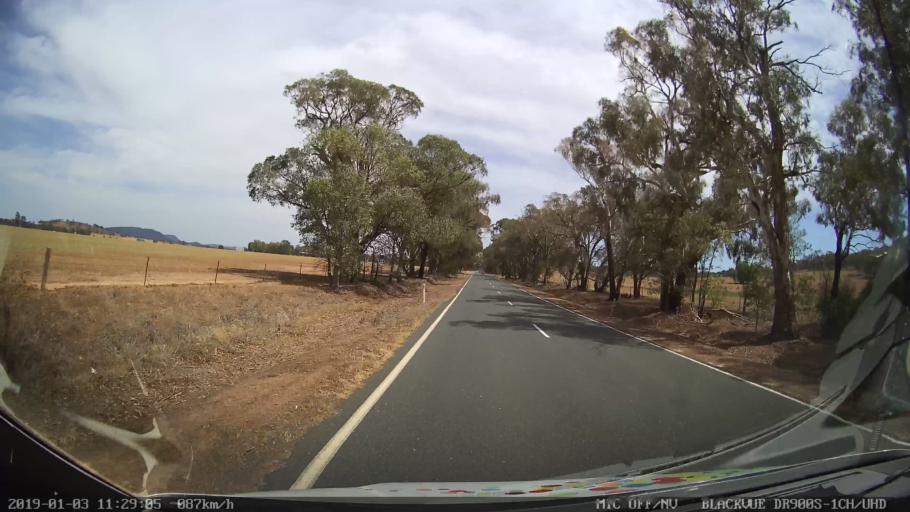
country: AU
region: New South Wales
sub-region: Weddin
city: Grenfell
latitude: -33.9958
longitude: 148.2020
